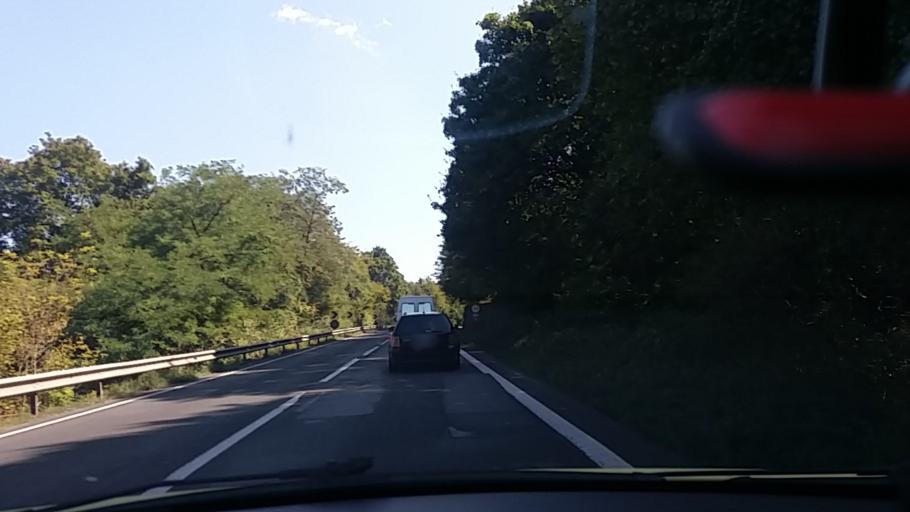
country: RO
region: Hunedoara
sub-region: Comuna Branisca
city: Branisca
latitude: 45.9197
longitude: 22.7181
